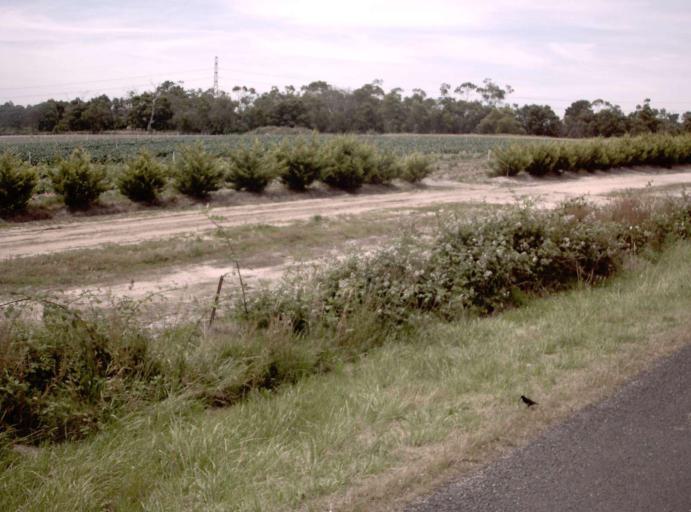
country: AU
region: Victoria
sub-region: Mornington Peninsula
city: Tyabb
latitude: -38.2500
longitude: 145.2150
